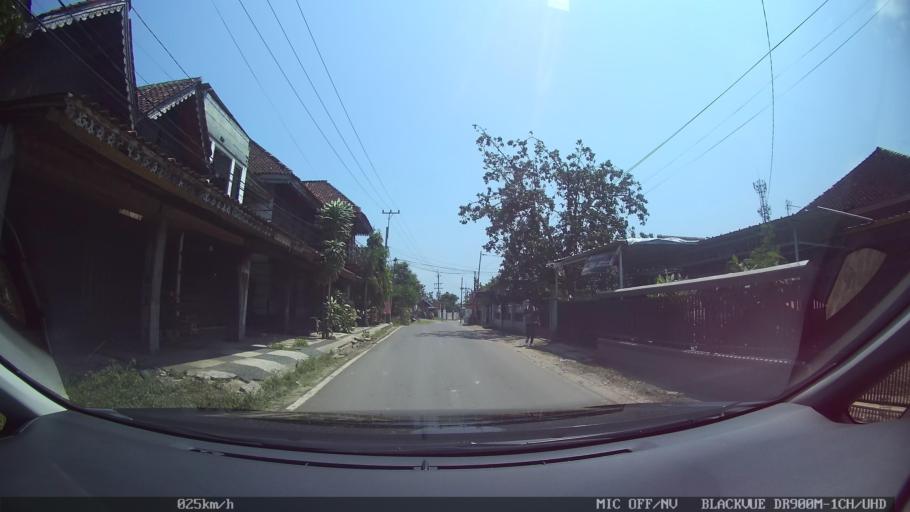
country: ID
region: Lampung
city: Kedaton
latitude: -5.3654
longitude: 105.2719
